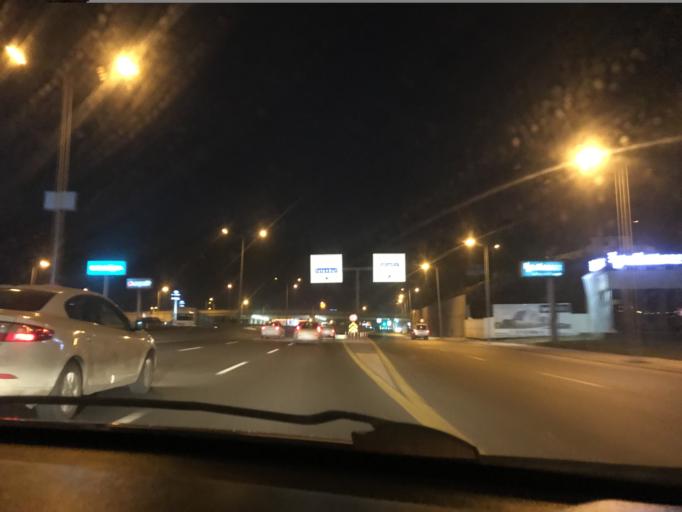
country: TR
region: Ankara
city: Batikent
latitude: 39.9454
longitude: 32.7154
